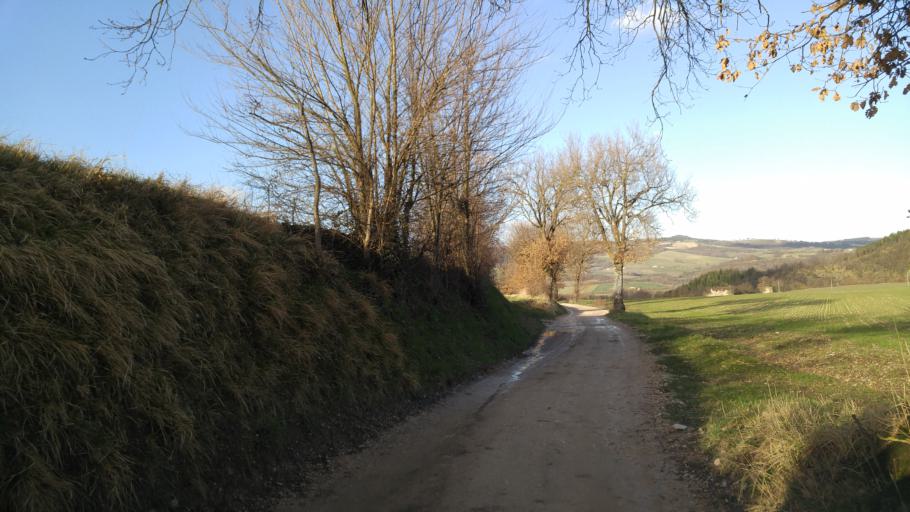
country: IT
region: The Marches
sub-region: Provincia di Pesaro e Urbino
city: Cagli
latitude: 43.5343
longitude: 12.6929
